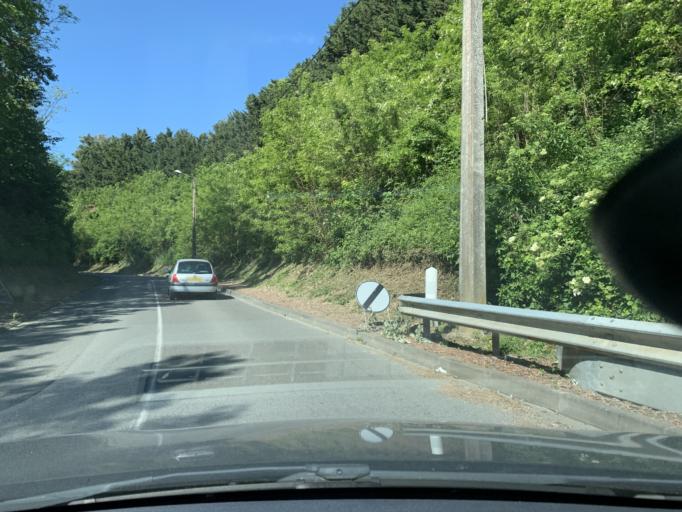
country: FR
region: Nord-Pas-de-Calais
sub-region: Departement du Nord
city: Rumilly-en-Cambresis
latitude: 50.1010
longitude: 3.2457
